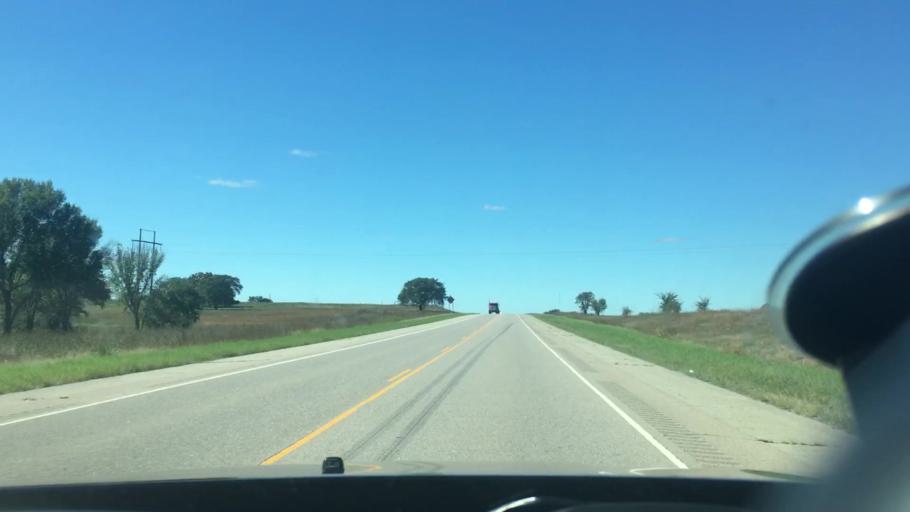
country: US
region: Oklahoma
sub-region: Coal County
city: Coalgate
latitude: 34.6171
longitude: -96.4476
